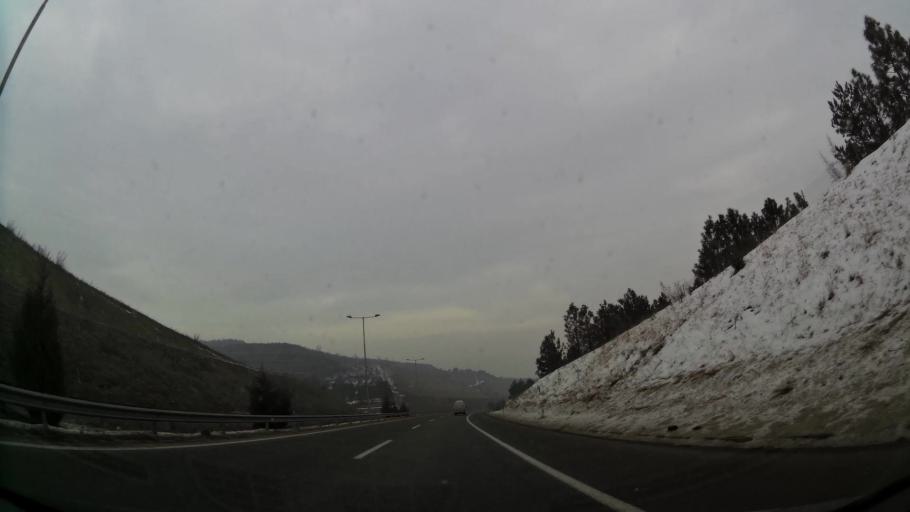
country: MK
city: Kondovo
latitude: 42.0530
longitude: 21.3400
